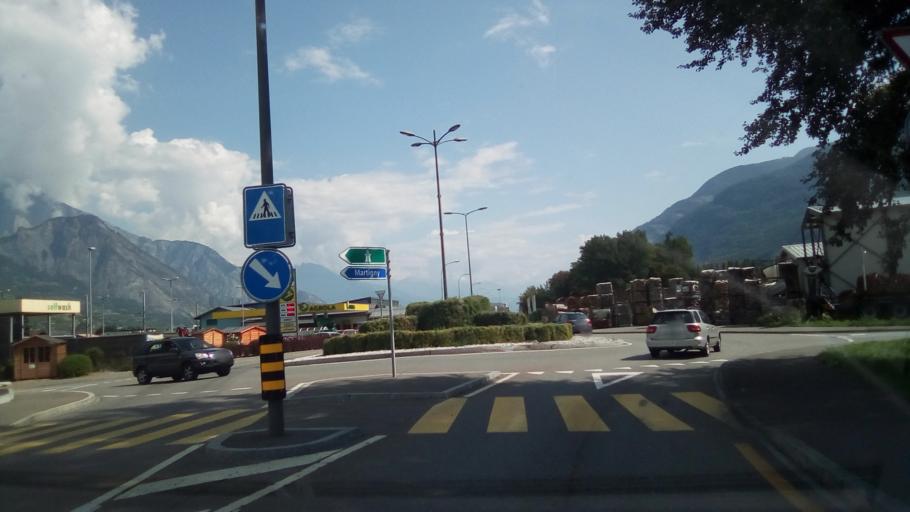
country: CH
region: Valais
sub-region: Martigny District
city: Saxon
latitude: 46.1456
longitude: 7.1673
